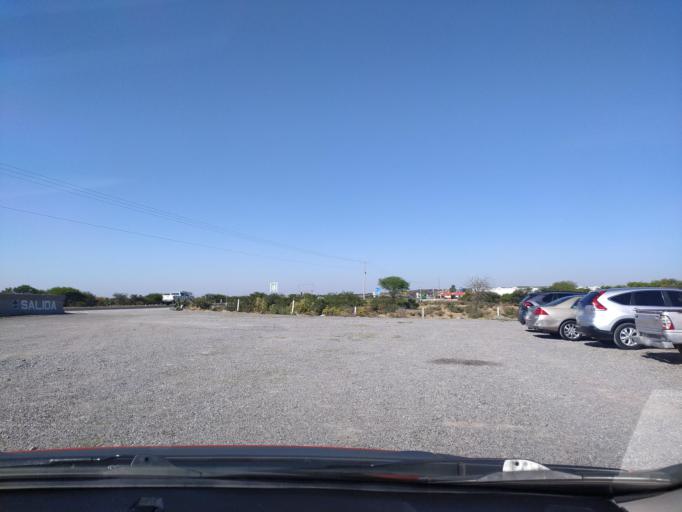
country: MX
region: Jalisco
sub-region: Lagos de Moreno
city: Cristeros [Fraccionamiento]
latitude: 21.2979
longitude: -102.1327
